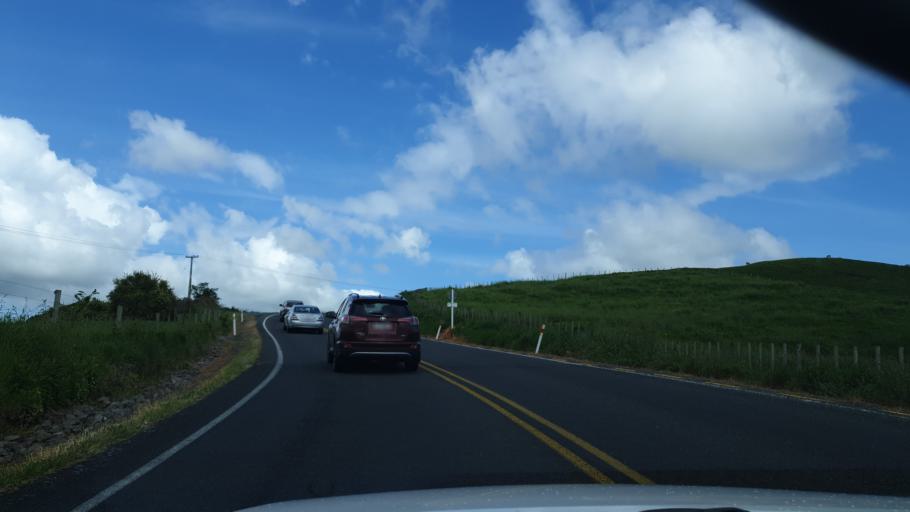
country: NZ
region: Waikato
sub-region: Matamata-Piako District
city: Matamata
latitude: -37.8791
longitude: 175.6918
